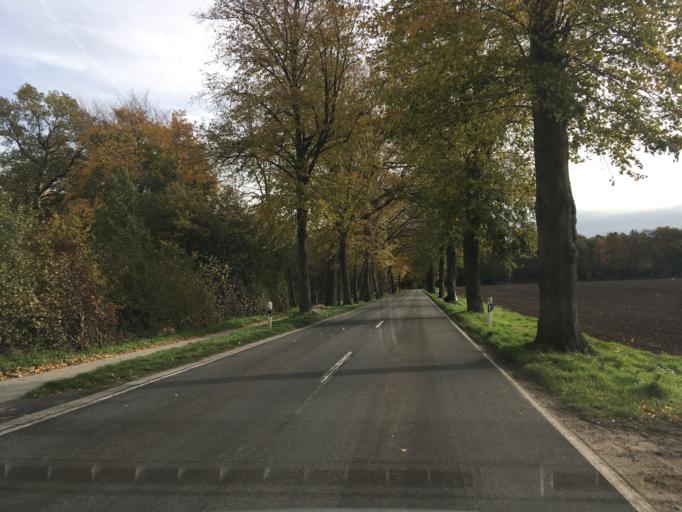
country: DE
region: North Rhine-Westphalia
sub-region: Regierungsbezirk Munster
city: Klein Reken
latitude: 51.8455
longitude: 7.0841
